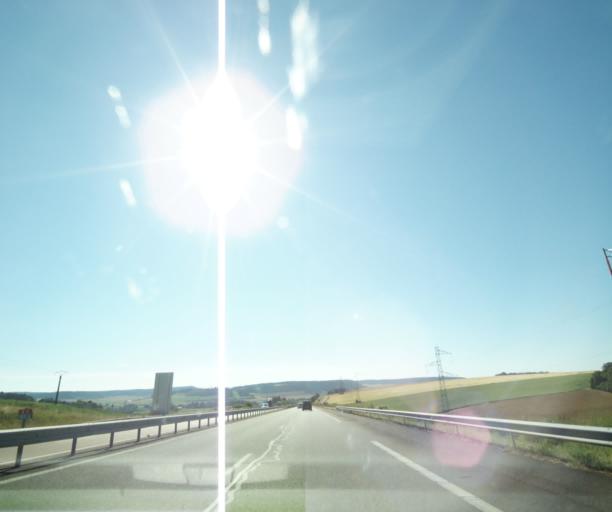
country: FR
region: Champagne-Ardenne
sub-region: Departement de la Haute-Marne
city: Chateauvillain
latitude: 48.0806
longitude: 4.8686
